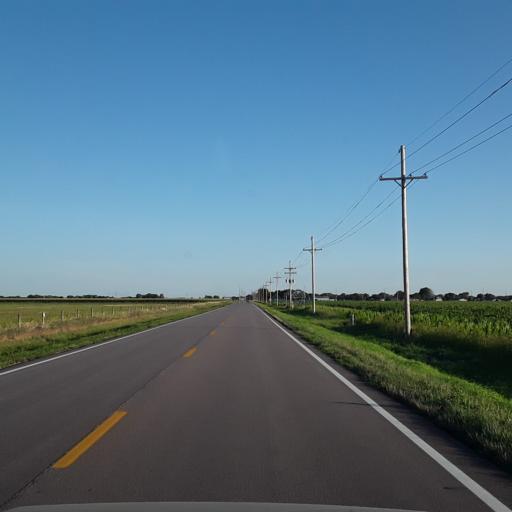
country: US
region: Nebraska
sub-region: Hall County
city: Grand Island
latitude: 40.9543
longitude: -98.3207
